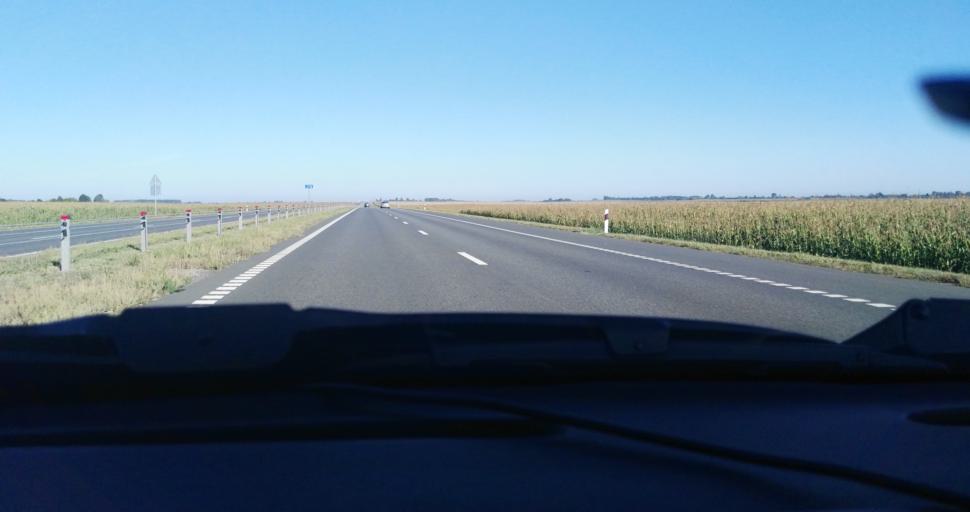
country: BY
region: Gomel
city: Buda-Kashalyova
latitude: 52.5251
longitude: 30.6178
